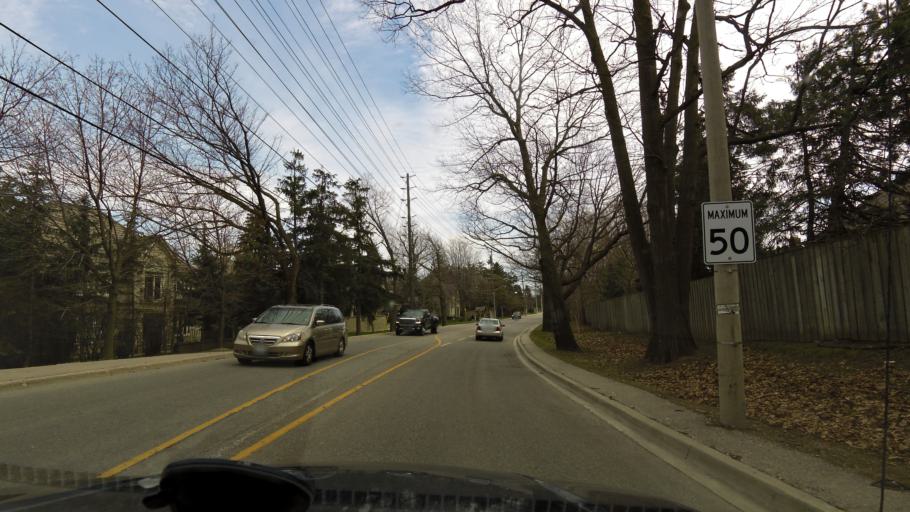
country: CA
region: Ontario
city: Mississauga
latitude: 43.5529
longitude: -79.6747
